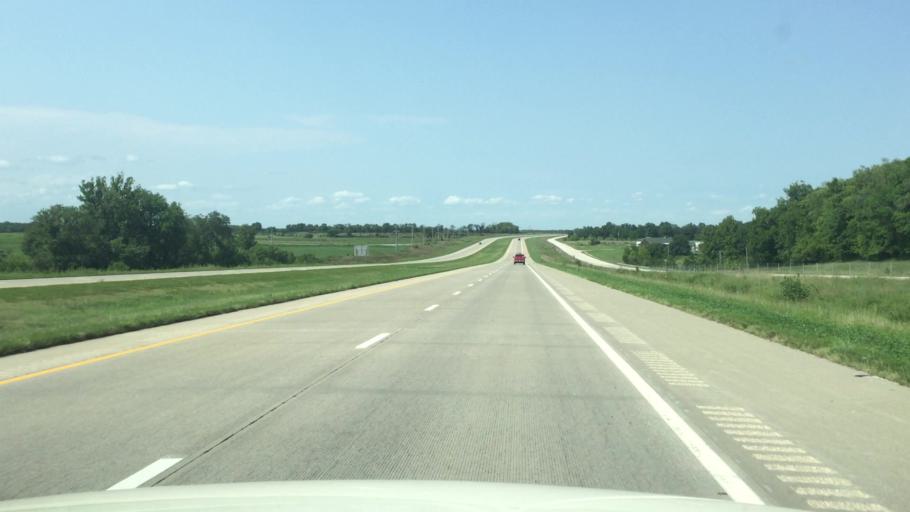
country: US
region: Kansas
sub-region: Linn County
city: Pleasanton
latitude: 38.1989
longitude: -94.7053
